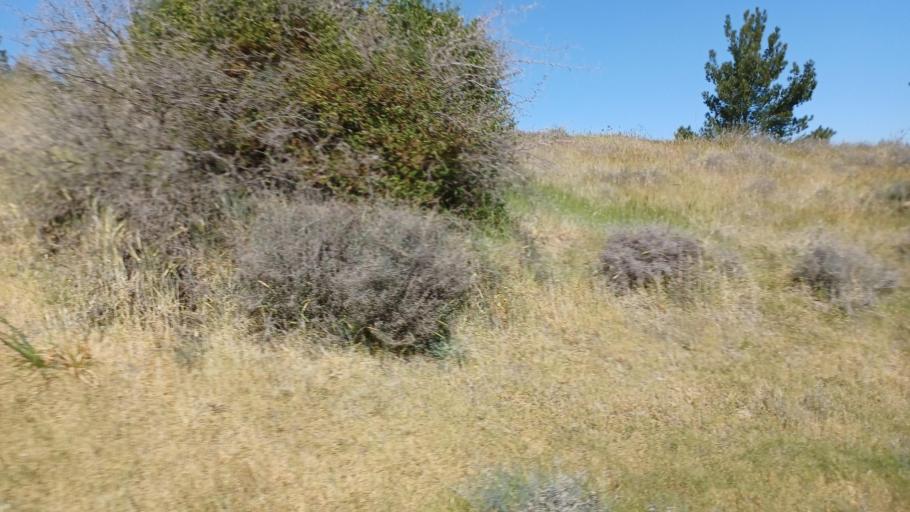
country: CY
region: Lefkosia
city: Peristerona
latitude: 35.0631
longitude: 33.0574
